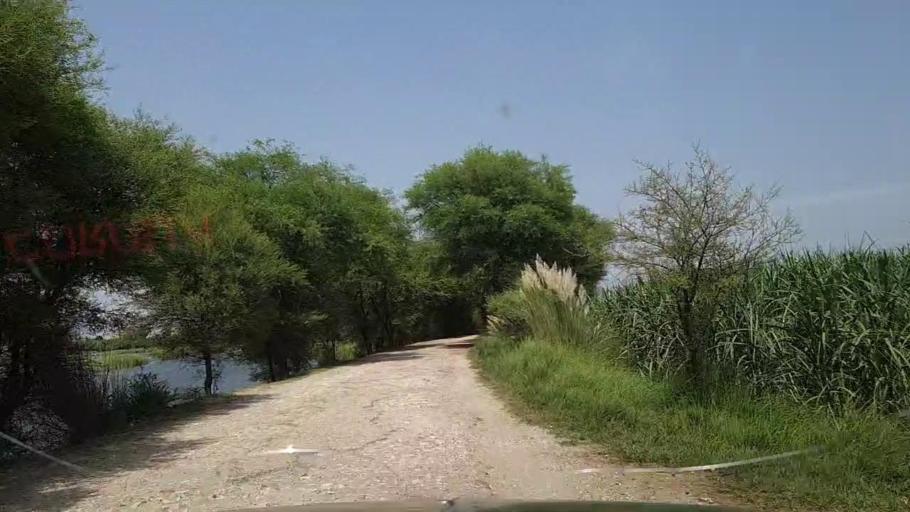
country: PK
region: Sindh
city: Ghotki
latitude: 28.0909
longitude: 69.3118
